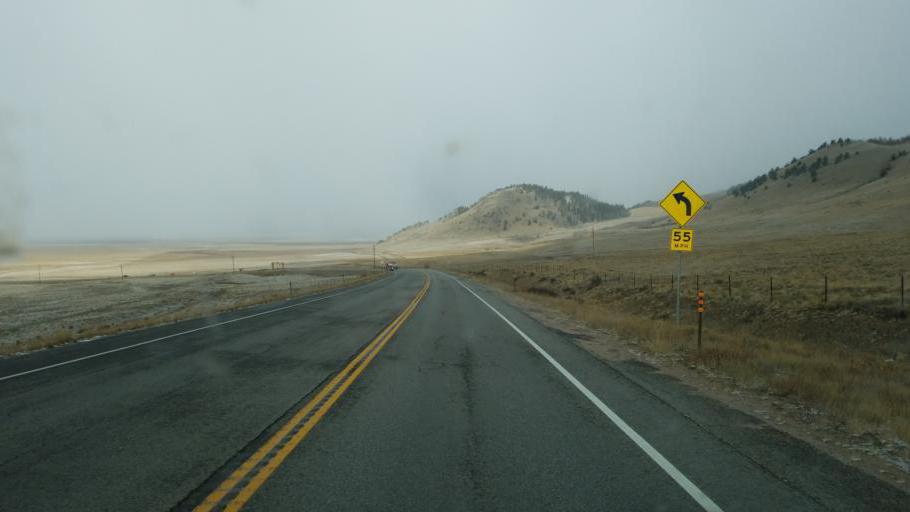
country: US
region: Colorado
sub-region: Summit County
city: Breckenridge
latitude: 39.4055
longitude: -105.7698
